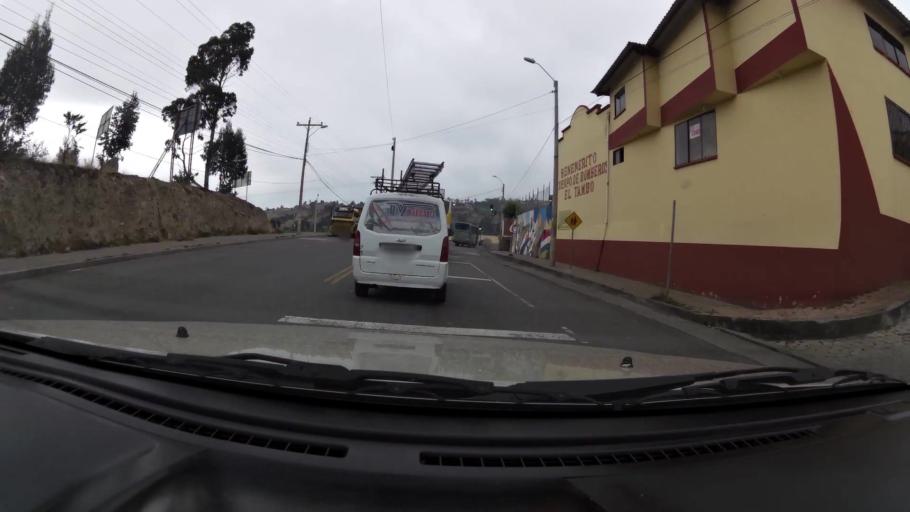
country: EC
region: Canar
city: Canar
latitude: -2.5130
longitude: -78.9292
